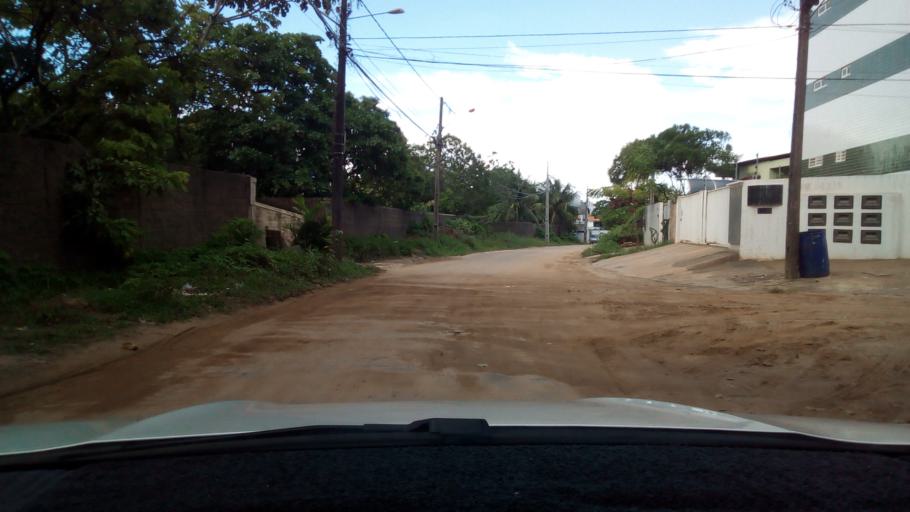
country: BR
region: Paraiba
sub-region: Joao Pessoa
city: Joao Pessoa
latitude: -7.1566
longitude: -34.8491
